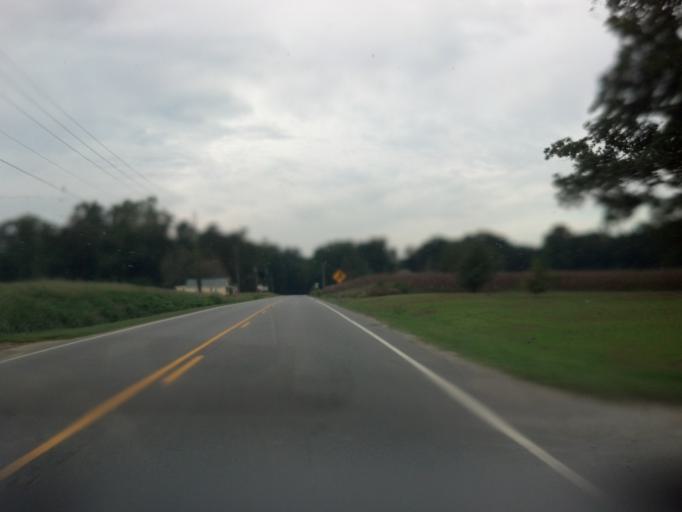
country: US
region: North Carolina
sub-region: Pitt County
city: Ayden
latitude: 35.4745
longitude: -77.4671
